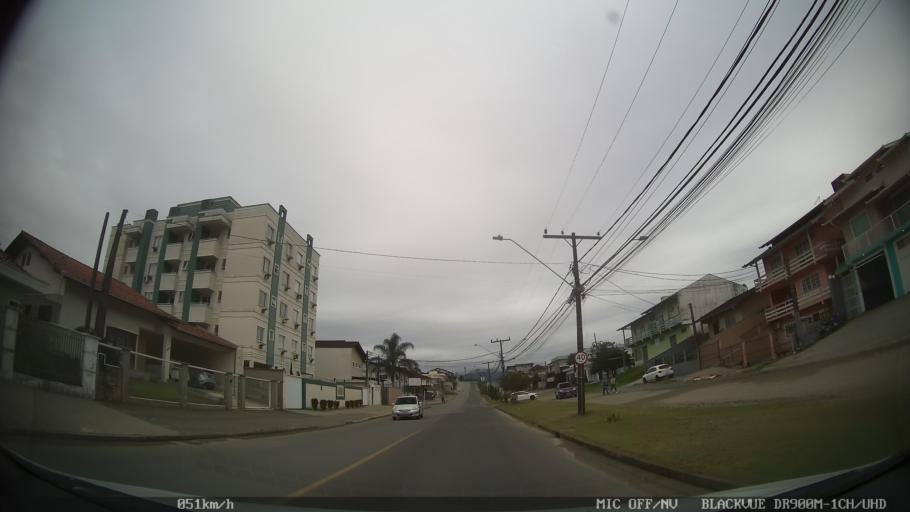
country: BR
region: Santa Catarina
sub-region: Joinville
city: Joinville
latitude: -26.2741
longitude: -48.8868
